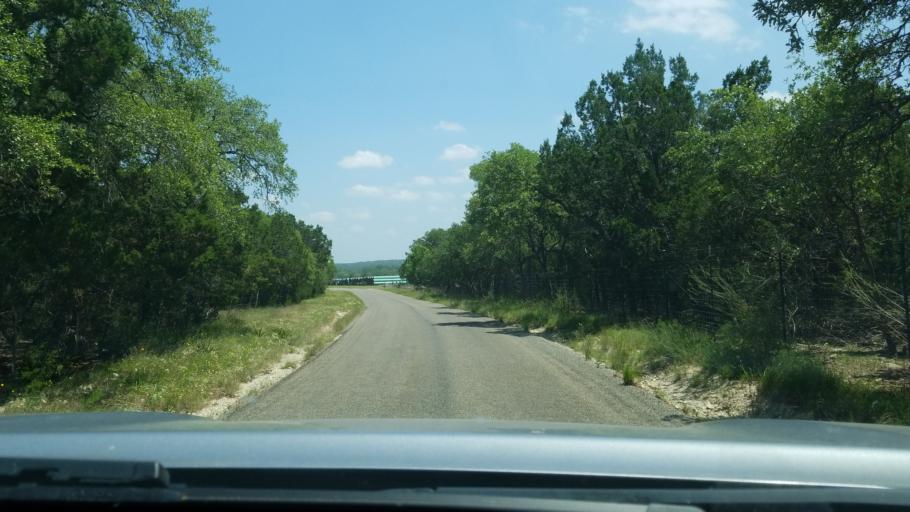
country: US
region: Texas
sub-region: Blanco County
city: Blanco
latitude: 30.0778
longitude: -98.4001
